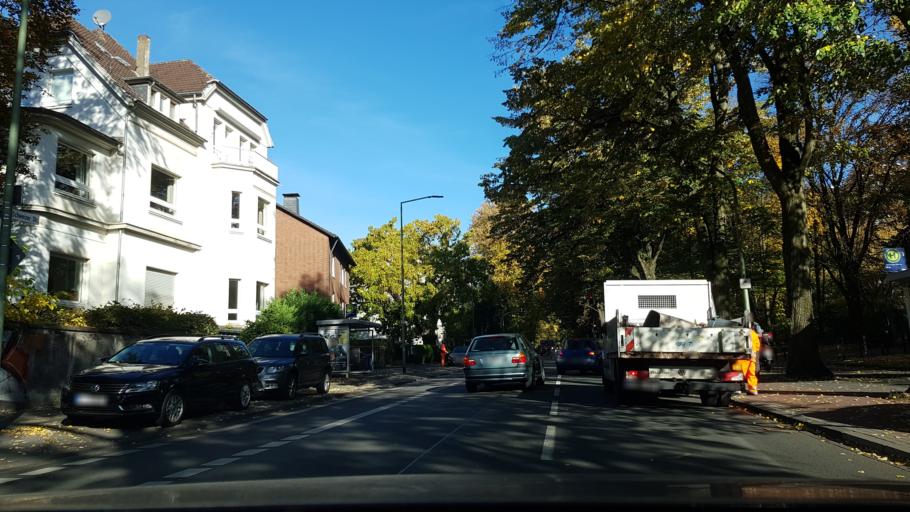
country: DE
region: North Rhine-Westphalia
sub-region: Regierungsbezirk Dusseldorf
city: Duisburg
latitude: 51.4354
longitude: 6.7962
